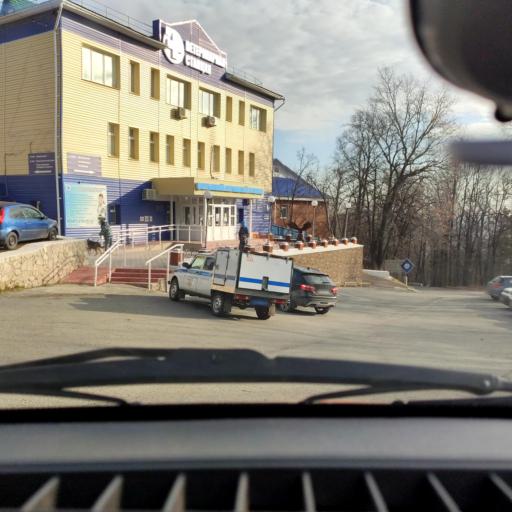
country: RU
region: Bashkortostan
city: Ufa
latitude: 54.7498
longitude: 56.0364
